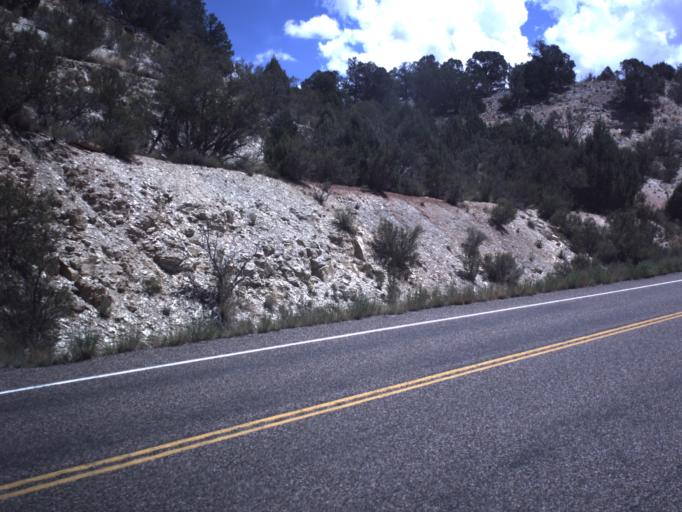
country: US
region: Utah
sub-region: Kane County
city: Kanab
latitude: 37.1979
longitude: -112.6674
